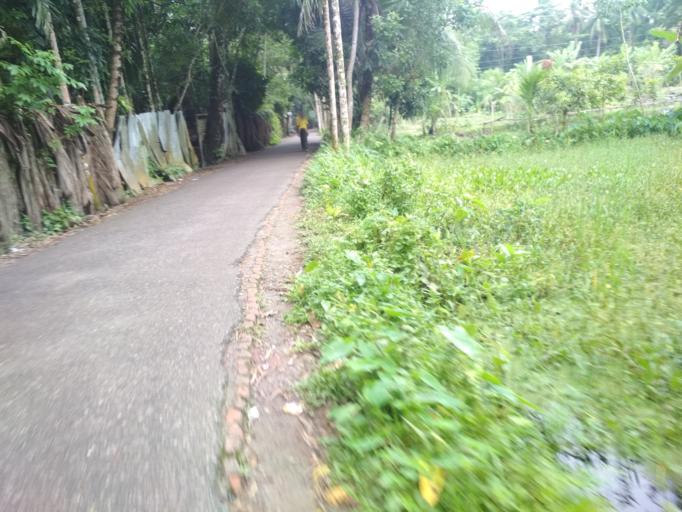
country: BD
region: Chittagong
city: Lakshmipur
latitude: 22.9661
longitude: 90.8017
